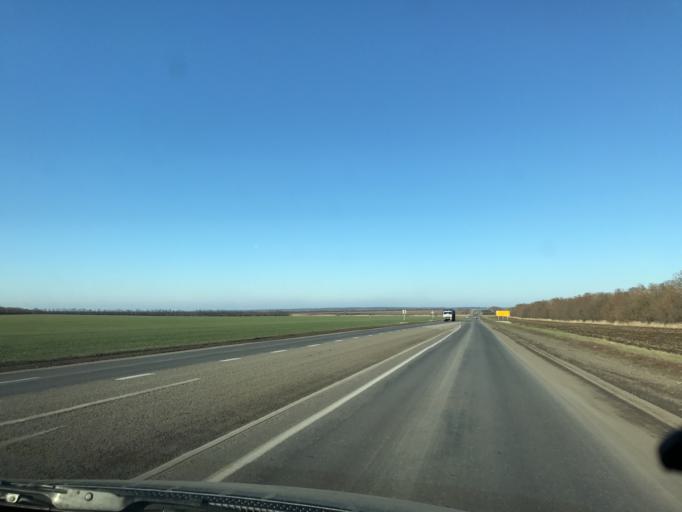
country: RU
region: Rostov
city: Kagal'nitskaya
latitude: 46.8496
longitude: 40.2059
